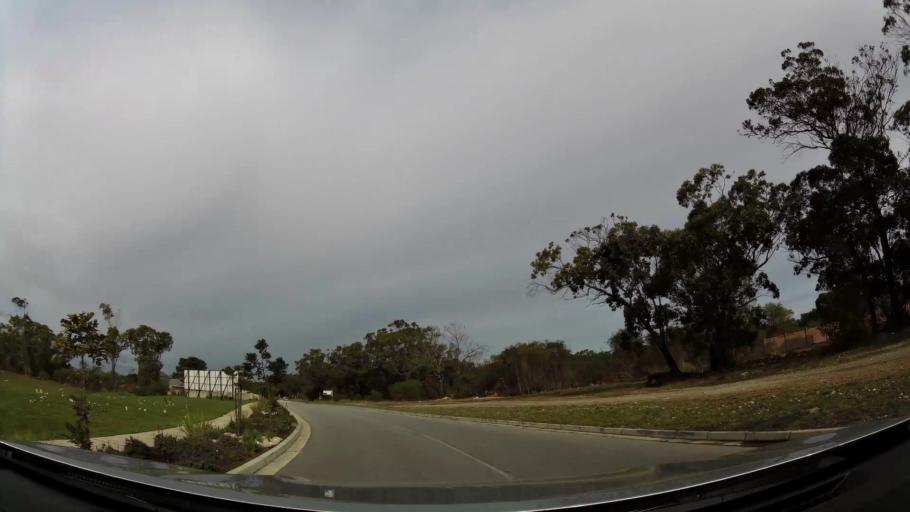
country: ZA
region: Eastern Cape
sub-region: Nelson Mandela Bay Metropolitan Municipality
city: Port Elizabeth
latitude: -33.9340
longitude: 25.4902
